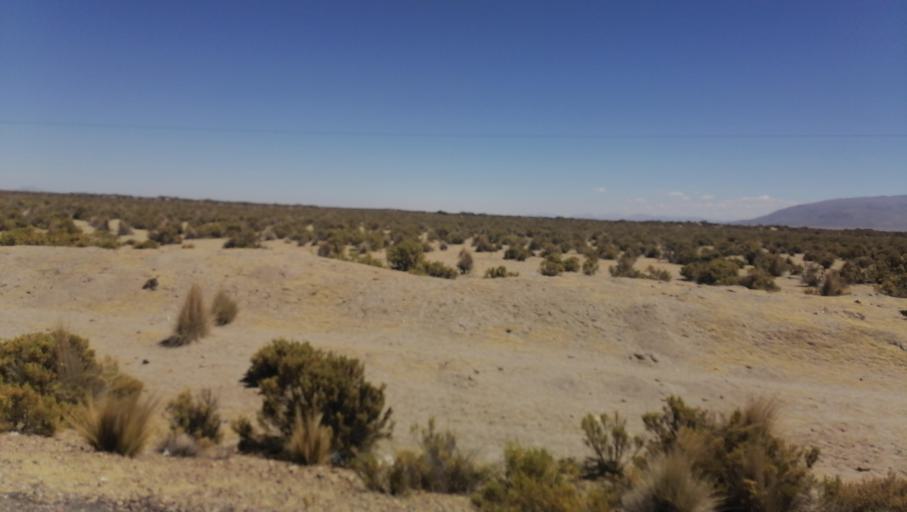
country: BO
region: Oruro
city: Challapata
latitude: -19.1703
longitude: -66.7840
